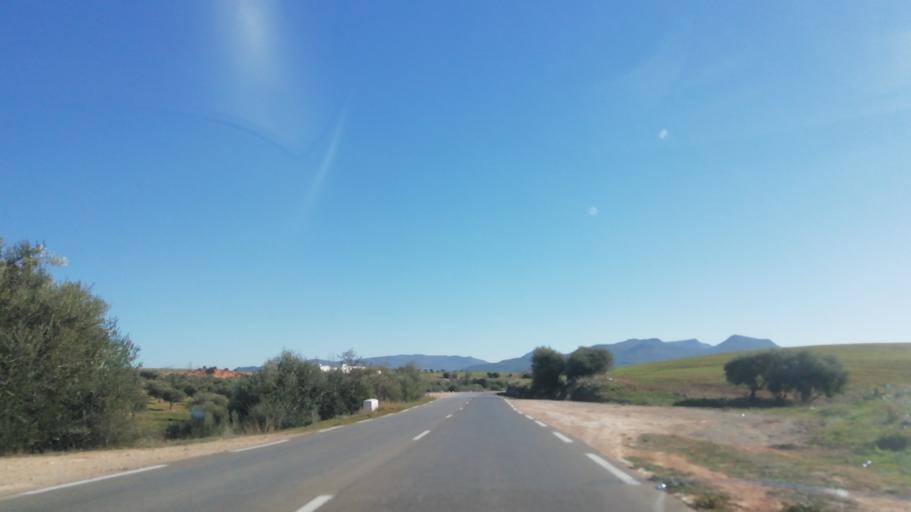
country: DZ
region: Tlemcen
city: Beni Mester
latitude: 34.8255
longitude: -1.5707
